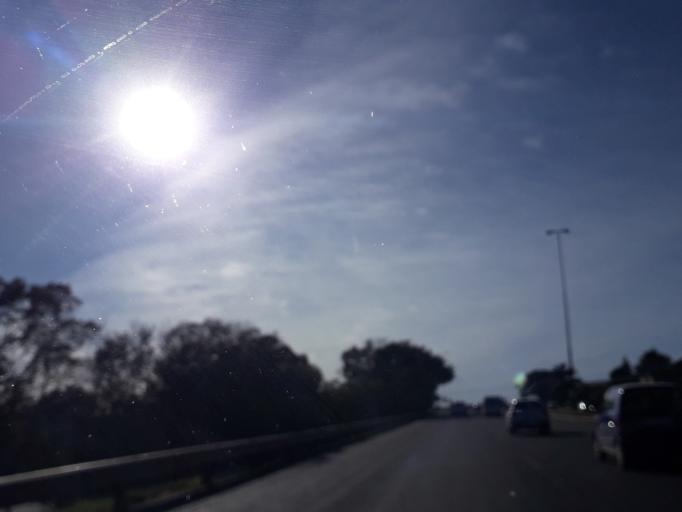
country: ZA
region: Gauteng
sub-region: City of Johannesburg Metropolitan Municipality
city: Roodepoort
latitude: -26.1604
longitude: 27.9308
